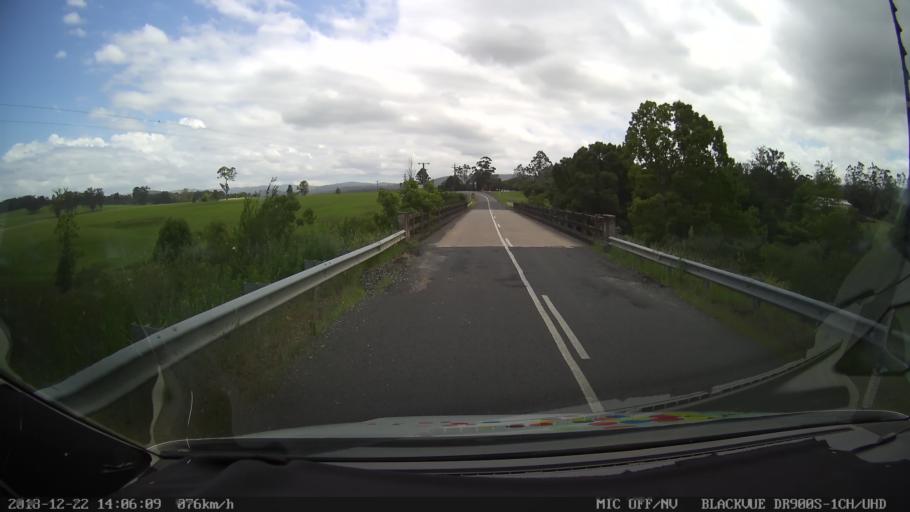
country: AU
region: New South Wales
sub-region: Clarence Valley
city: Coutts Crossing
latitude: -29.9526
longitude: 152.7284
